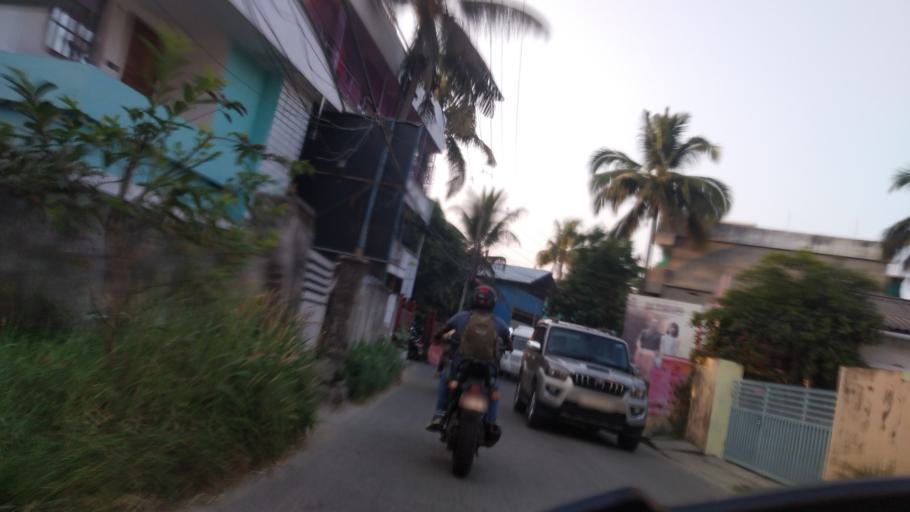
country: IN
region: Kerala
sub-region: Ernakulam
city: Elur
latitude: 10.0344
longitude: 76.2759
